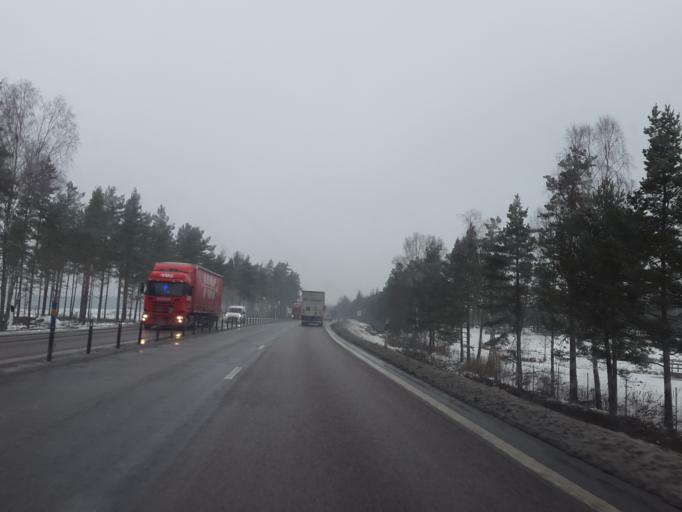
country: SE
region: Joenkoeping
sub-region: Jonkopings Kommun
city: Jonkoping
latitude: 57.7685
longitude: 14.0891
